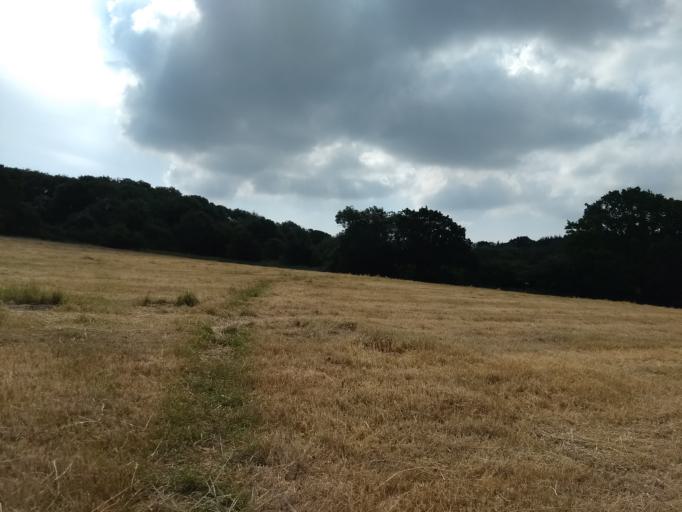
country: GB
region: England
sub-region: Isle of Wight
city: Ryde
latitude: 50.7104
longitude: -1.1524
